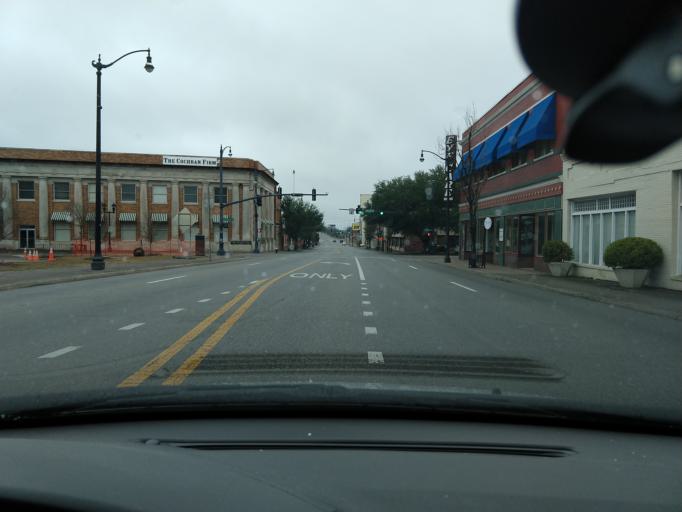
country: US
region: Alabama
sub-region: Houston County
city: Dothan
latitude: 31.2237
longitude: -85.3927
